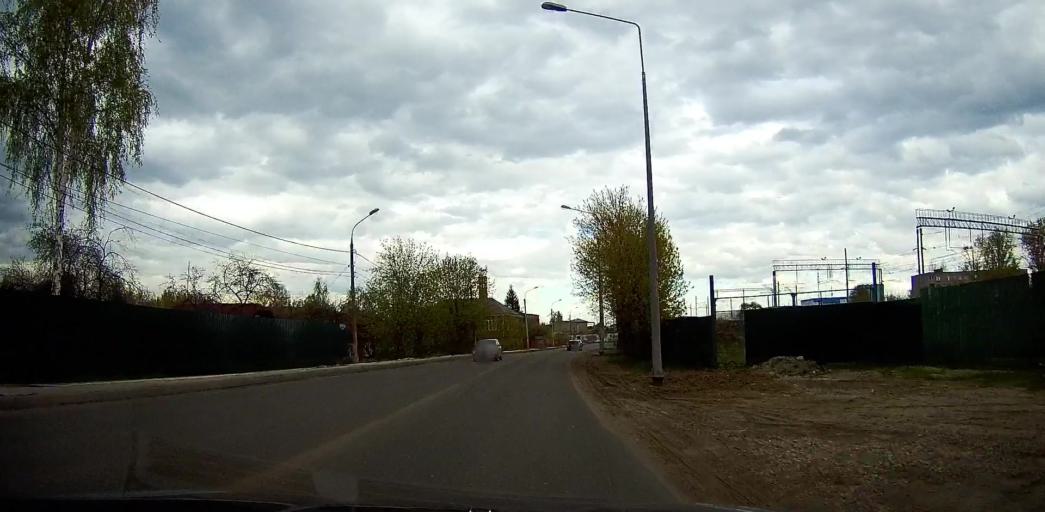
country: RU
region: Moskovskaya
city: Pavlovskiy Posad
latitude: 55.7760
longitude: 38.6834
